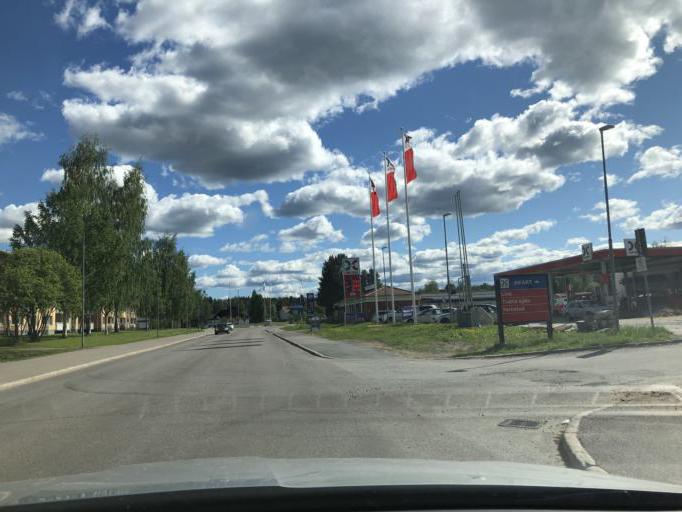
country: SE
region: Norrbotten
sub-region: Alvsbyns Kommun
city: AElvsbyn
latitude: 65.6733
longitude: 21.0058
